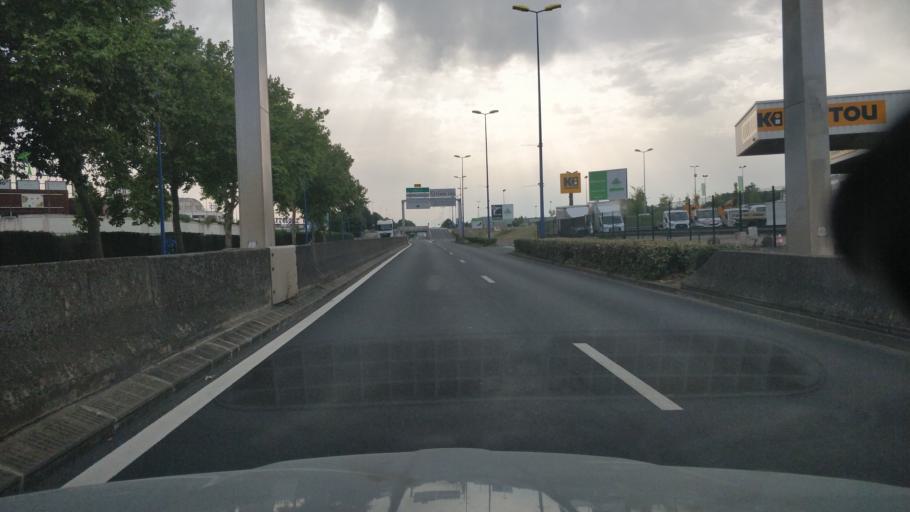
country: FR
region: Ile-de-France
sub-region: Departement de Seine-et-Marne
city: Brou-sur-Chantereine
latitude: 48.8788
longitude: 2.6181
